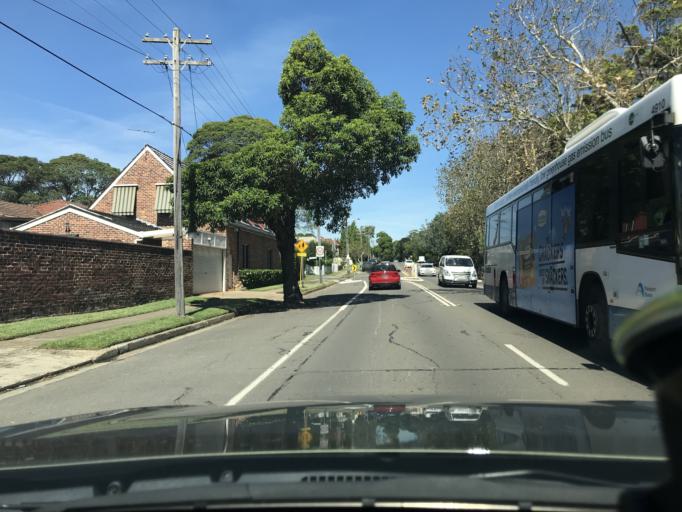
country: AU
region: New South Wales
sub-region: Canada Bay
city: Concord
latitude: -33.8625
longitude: 151.1054
